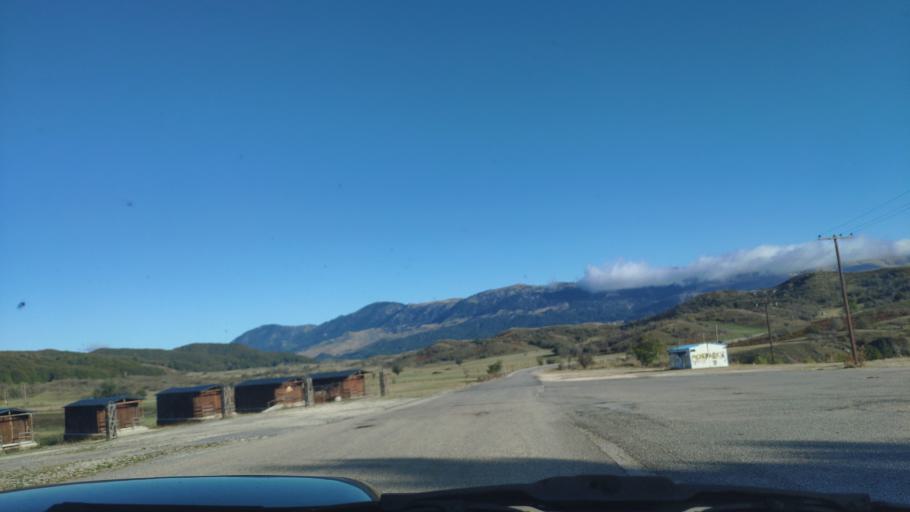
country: GR
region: Epirus
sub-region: Nomos Ioanninon
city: Metsovo
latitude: 39.7847
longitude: 21.1590
